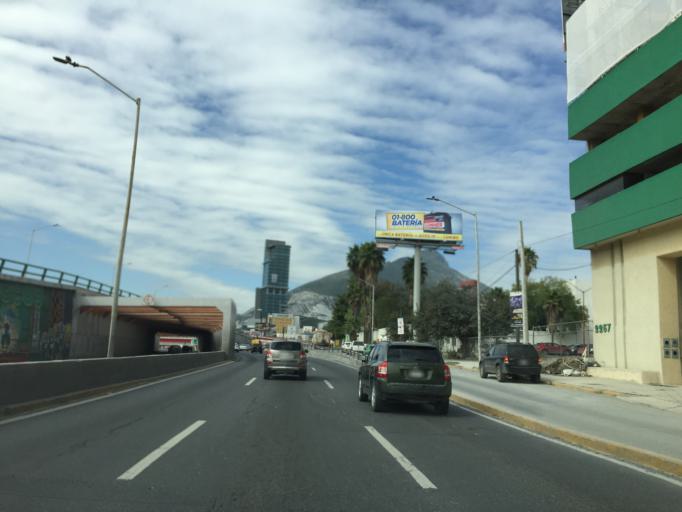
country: MX
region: Nuevo Leon
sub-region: Monterrey
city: Monterrey
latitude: 25.6715
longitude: -100.3485
